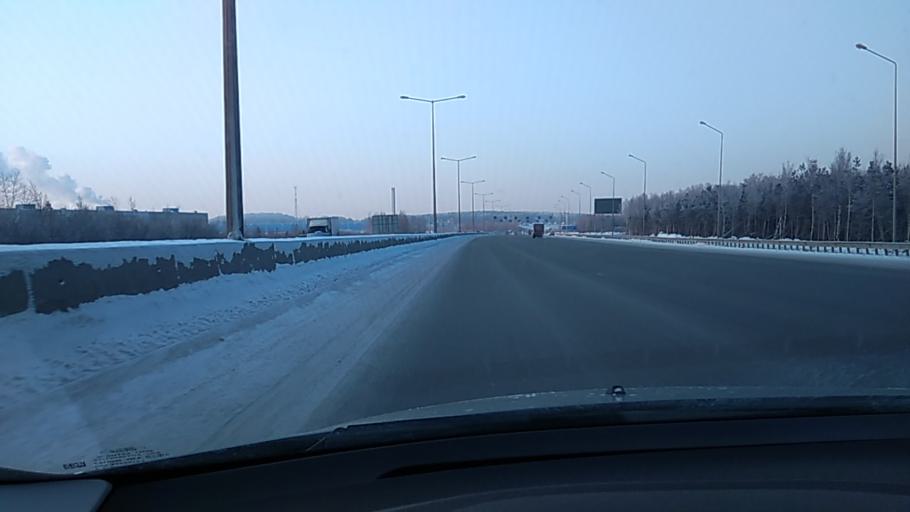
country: RU
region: Sverdlovsk
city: Istok
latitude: 56.7627
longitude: 60.7572
